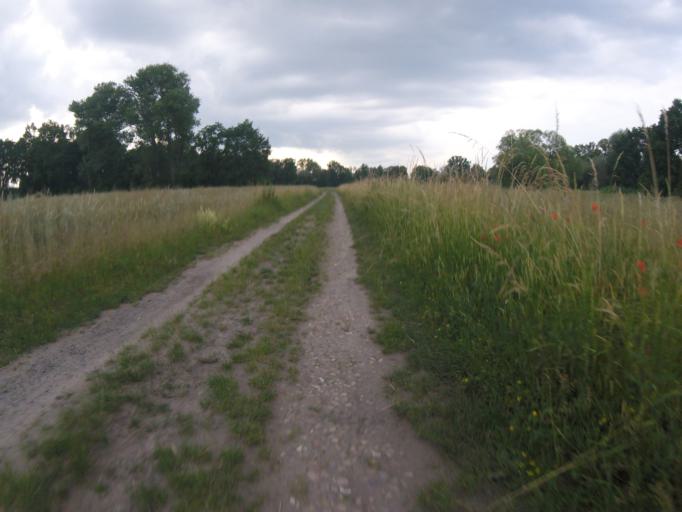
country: DE
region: Brandenburg
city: Mittenwalde
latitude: 52.2825
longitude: 13.5851
